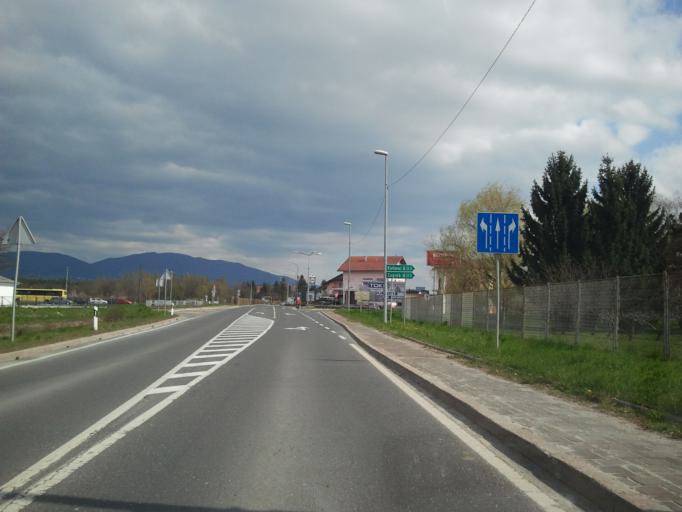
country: HR
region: Zagrebacka
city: Jastrebarsko
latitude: 45.6578
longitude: 15.6392
